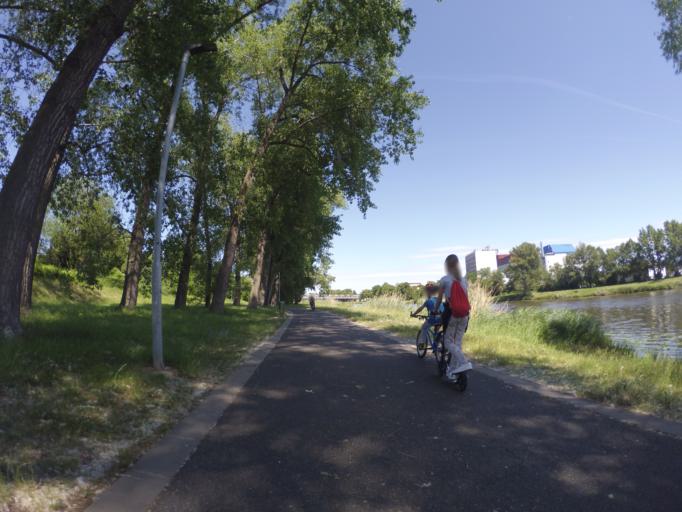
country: CZ
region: Central Bohemia
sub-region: Okres Nymburk
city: Nymburk
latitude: 50.1787
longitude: 15.0311
